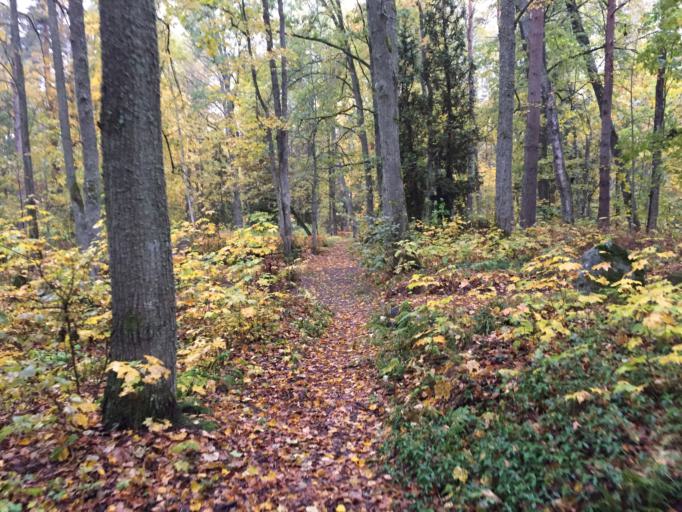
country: LV
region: Engure
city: Smarde
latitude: 56.9182
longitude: 23.4672
